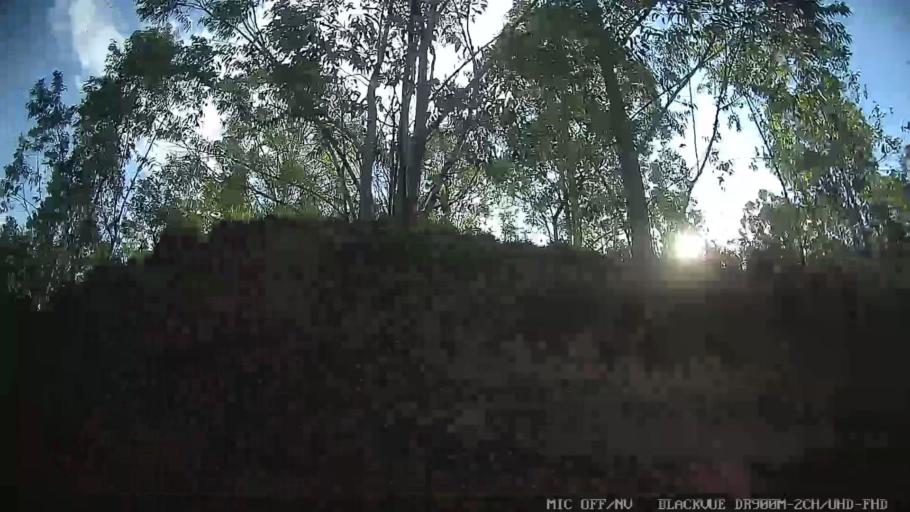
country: BR
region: Sao Paulo
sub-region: Serra Negra
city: Serra Negra
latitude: -22.6456
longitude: -46.6964
